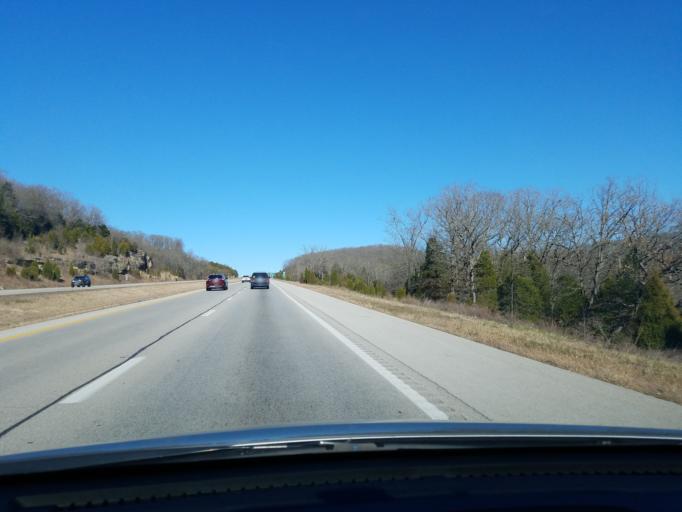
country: US
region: Missouri
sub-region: Taney County
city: Merriam Woods
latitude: 36.7831
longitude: -93.2245
